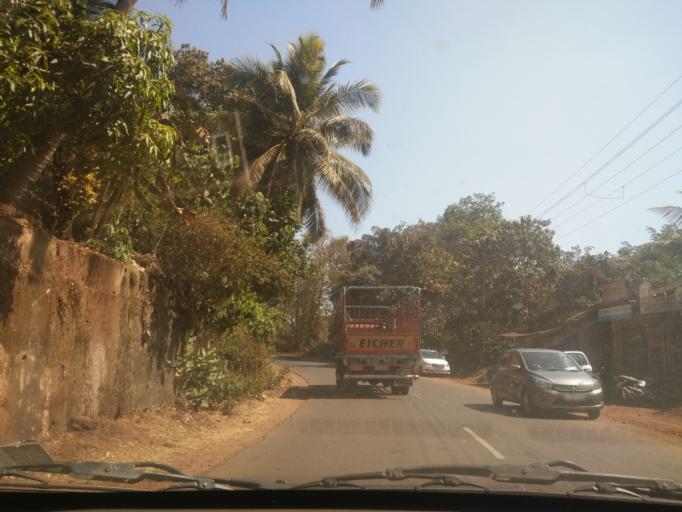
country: IN
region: Goa
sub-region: North Goa
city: Aldona
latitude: 15.6192
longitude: 73.9075
